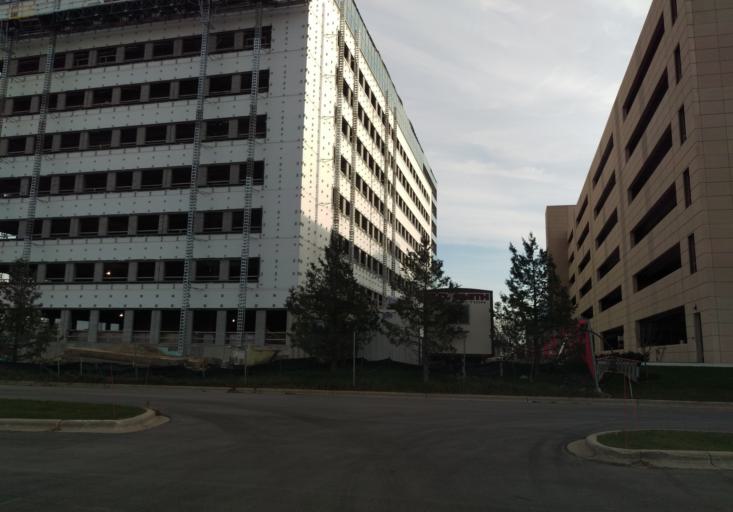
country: US
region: Wisconsin
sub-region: Dane County
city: Shorewood Hills
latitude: 43.0740
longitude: -89.4620
